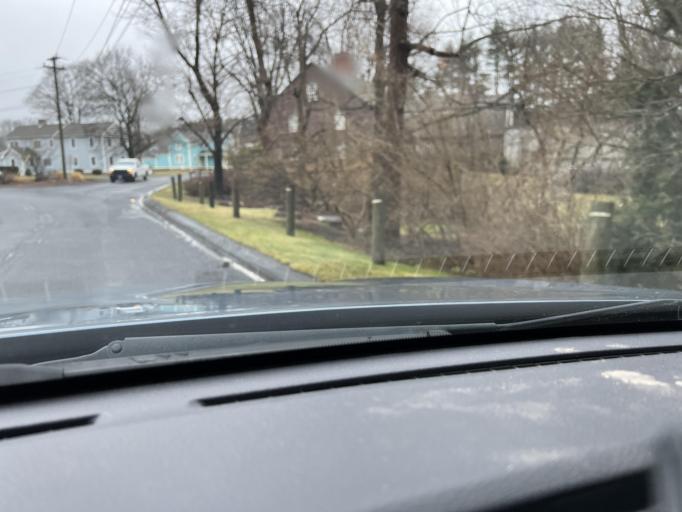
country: US
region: Massachusetts
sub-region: Hampden County
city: Southwick
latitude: 42.0365
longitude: -72.7126
